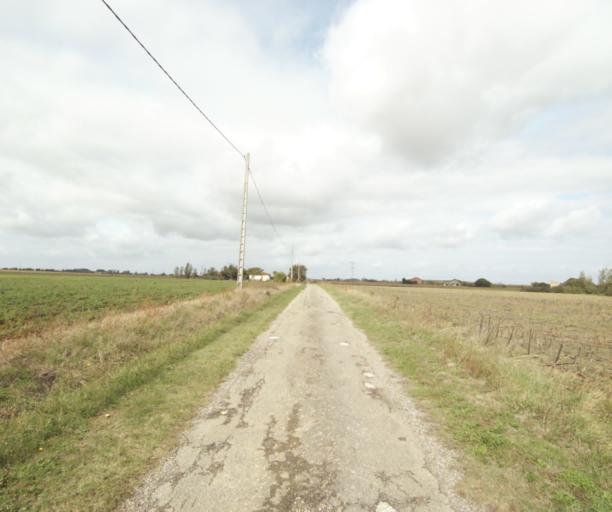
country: FR
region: Midi-Pyrenees
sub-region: Departement du Tarn-et-Garonne
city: Finhan
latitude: 43.8840
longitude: 1.1337
